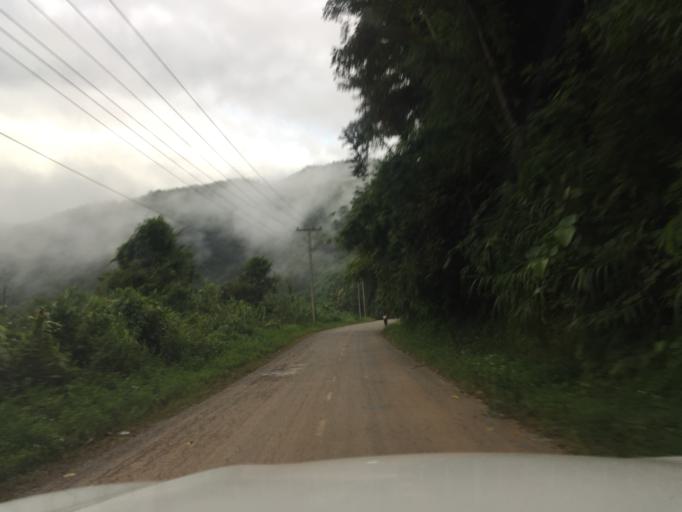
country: LA
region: Phongsali
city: Khoa
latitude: 21.0733
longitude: 102.3759
